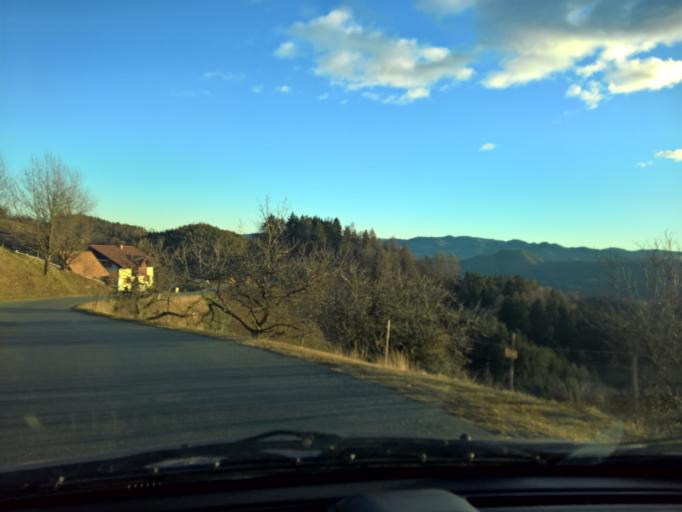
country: AT
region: Styria
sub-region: Politischer Bezirk Leibnitz
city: Sankt Johann im Saggautal
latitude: 46.6970
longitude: 15.4392
